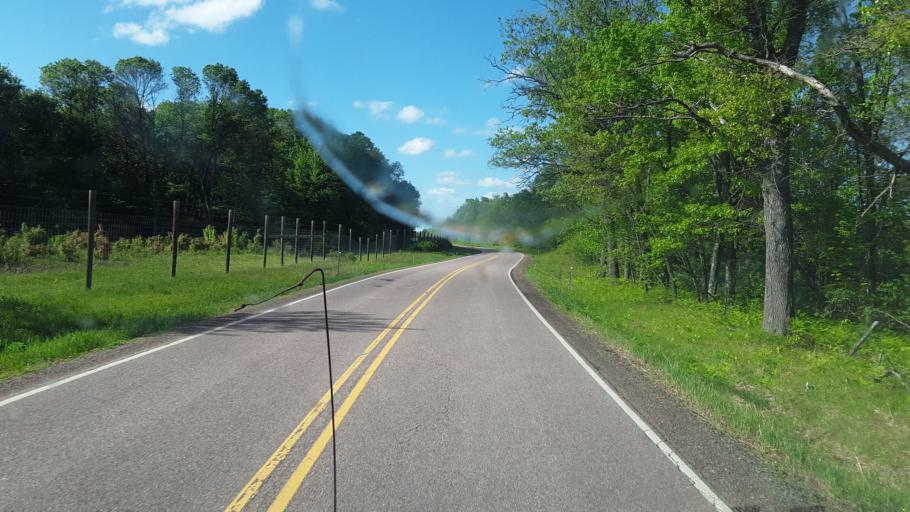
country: US
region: Wisconsin
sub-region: Wood County
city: Nekoosa
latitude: 44.3541
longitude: -90.1307
